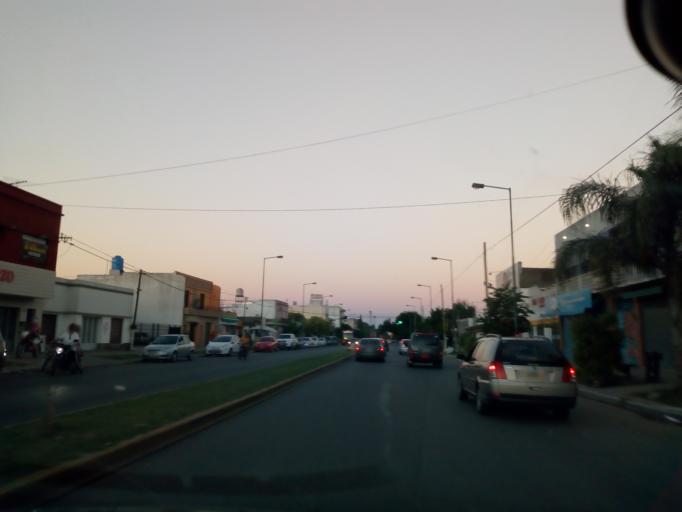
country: AR
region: Buenos Aires
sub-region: Partido de La Plata
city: La Plata
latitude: -34.9263
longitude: -57.9970
